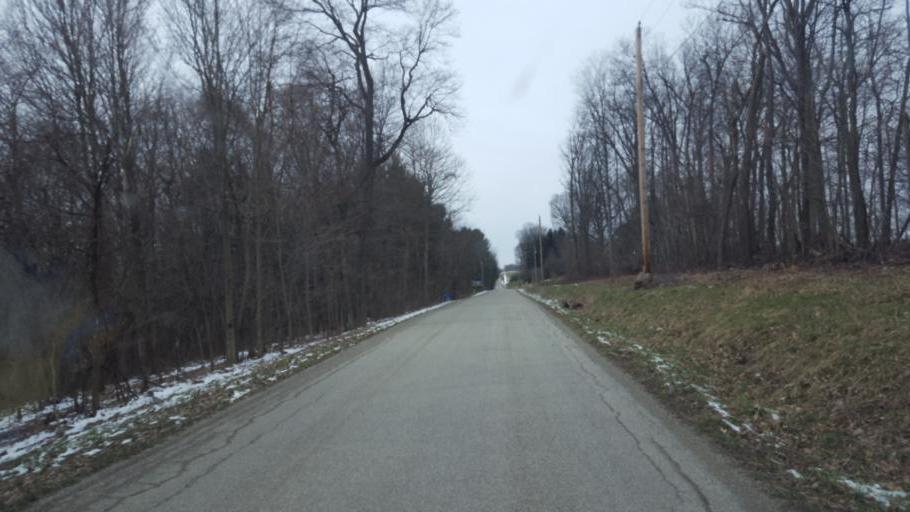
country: US
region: Ohio
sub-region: Sandusky County
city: Bellville
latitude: 40.5944
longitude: -82.5520
